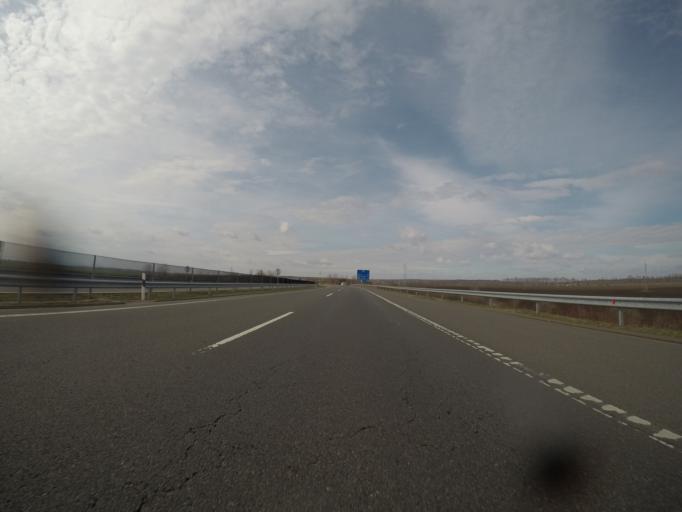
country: HU
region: Baranya
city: Boly
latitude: 45.9819
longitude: 18.5713
